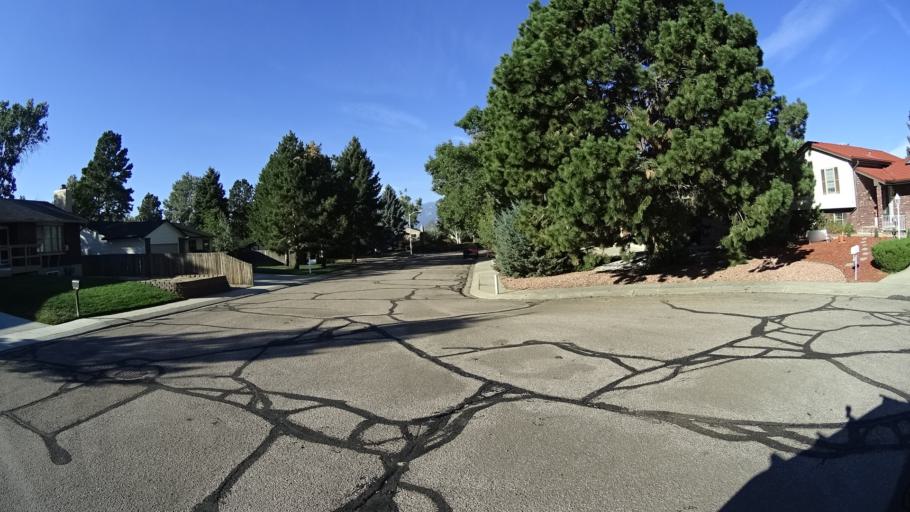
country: US
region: Colorado
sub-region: El Paso County
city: Cimarron Hills
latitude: 38.9080
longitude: -104.7550
